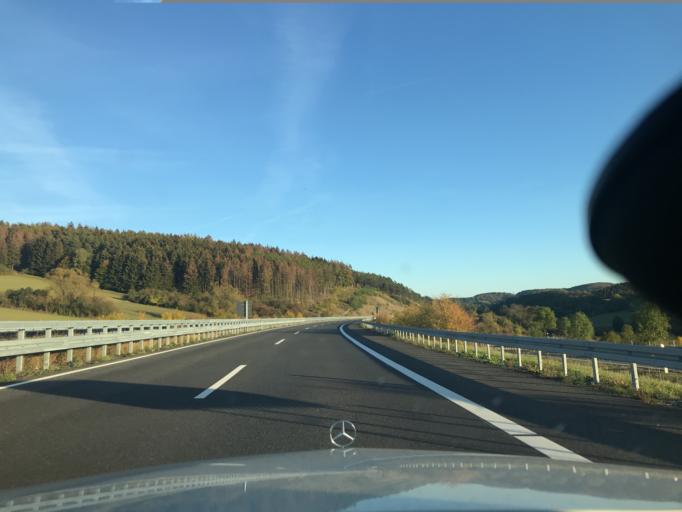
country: DE
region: Hesse
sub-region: Regierungsbezirk Kassel
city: Grossalmerode
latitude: 51.1930
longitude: 9.7875
